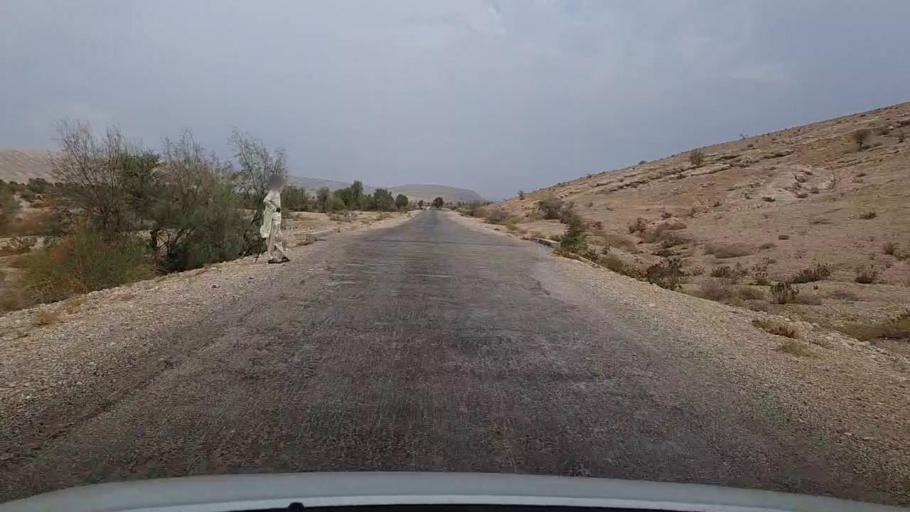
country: PK
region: Sindh
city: Sehwan
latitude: 26.2225
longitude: 67.7134
